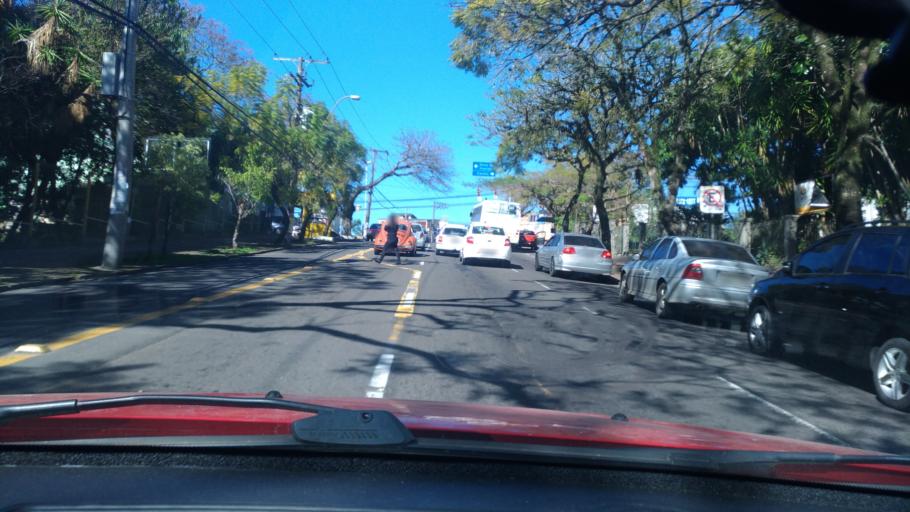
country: BR
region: Rio Grande do Sul
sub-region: Porto Alegre
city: Porto Alegre
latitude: -30.0420
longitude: -51.1452
